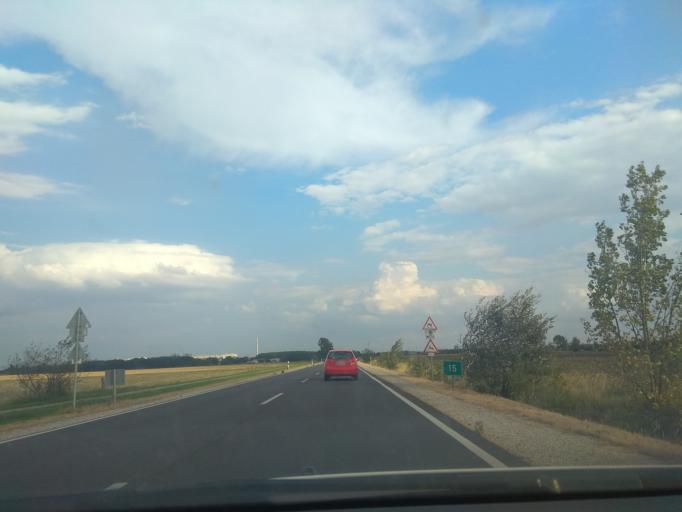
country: HU
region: Borsod-Abauj-Zemplen
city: Sajoszoged
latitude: 47.9367
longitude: 21.0090
